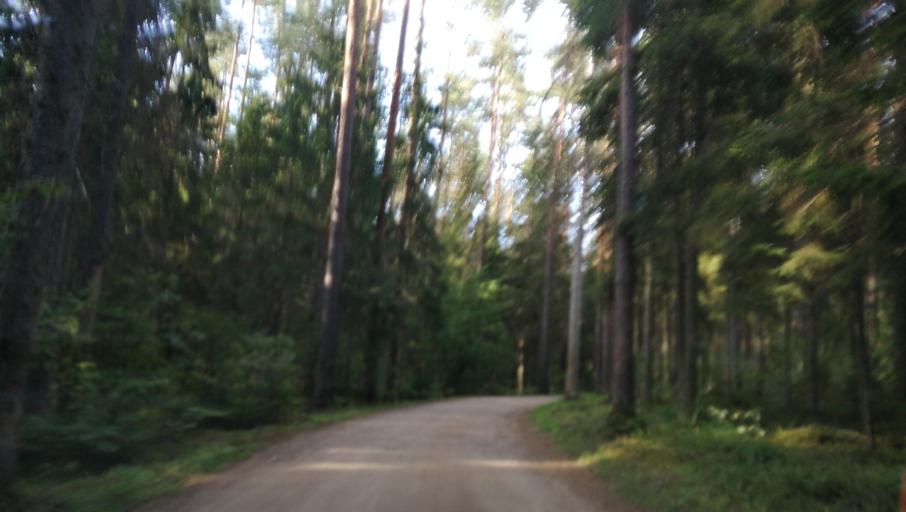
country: LV
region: Cesu Rajons
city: Cesis
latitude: 57.2913
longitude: 25.2128
